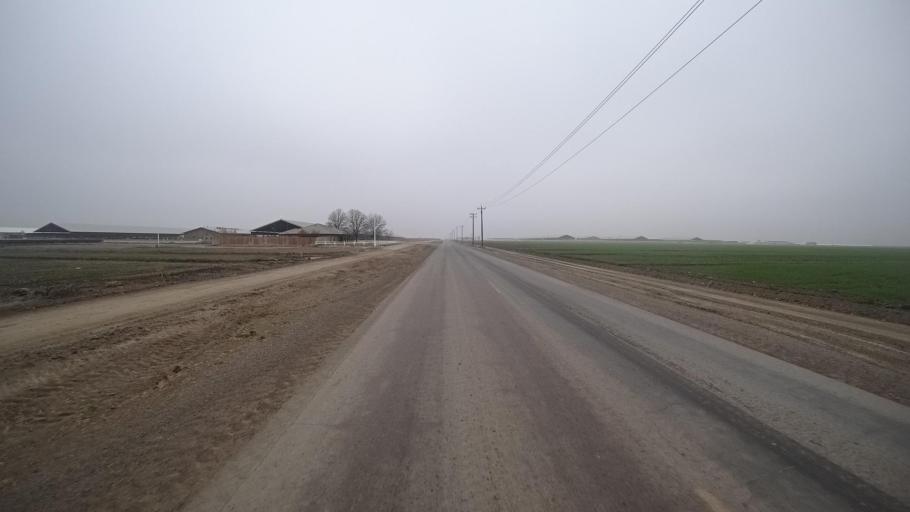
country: US
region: California
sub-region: Kern County
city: Rosedale
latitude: 35.2091
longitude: -119.1931
